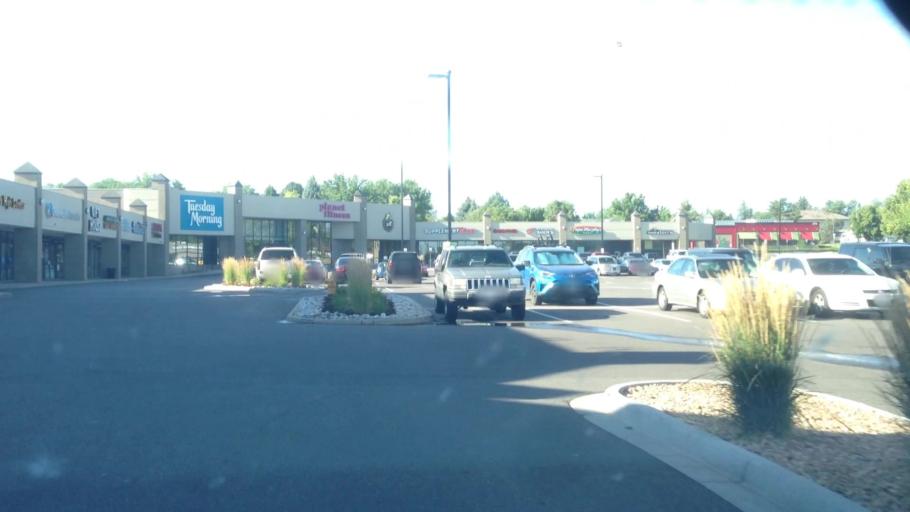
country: US
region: Colorado
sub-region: Jefferson County
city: Lakewood
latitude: 39.7173
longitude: -105.0801
